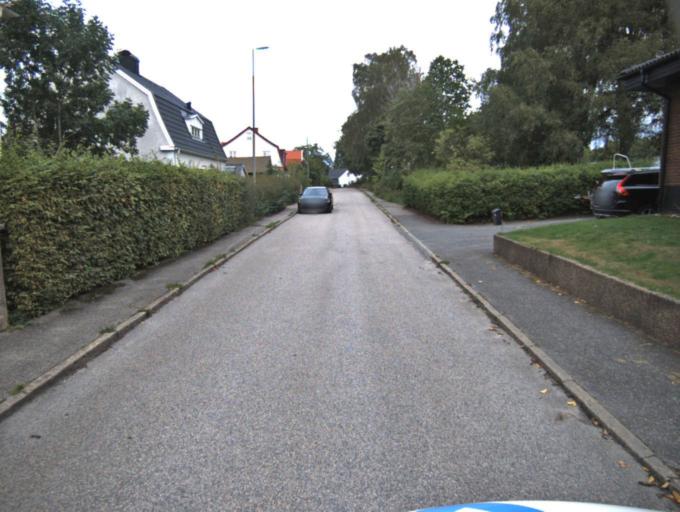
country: SE
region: Vaestra Goetaland
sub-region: Ulricehamns Kommun
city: Ulricehamn
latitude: 57.7935
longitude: 13.4217
